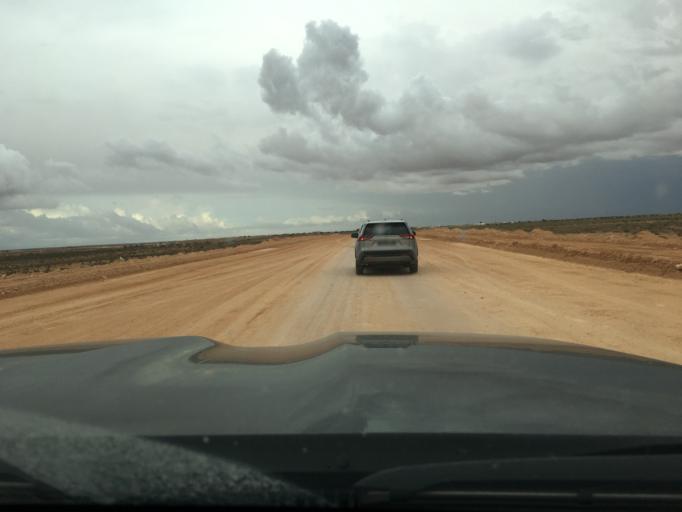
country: TN
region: Madanin
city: Medenine
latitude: 33.2821
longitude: 10.5959
